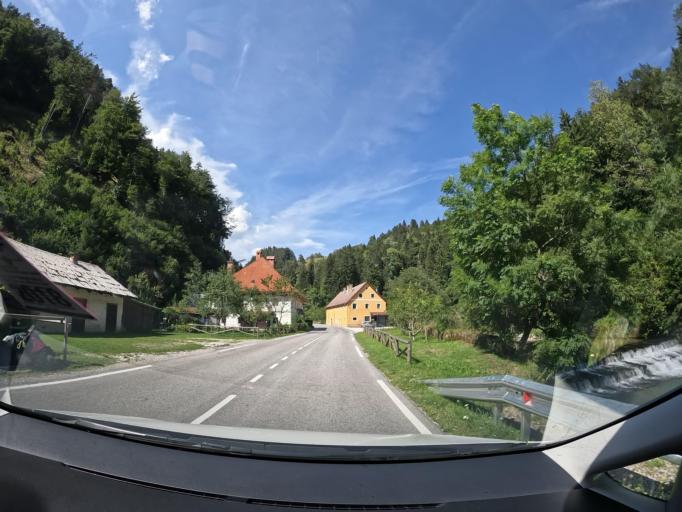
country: SI
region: Kranj
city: Golnik
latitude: 46.3809
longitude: 14.3885
